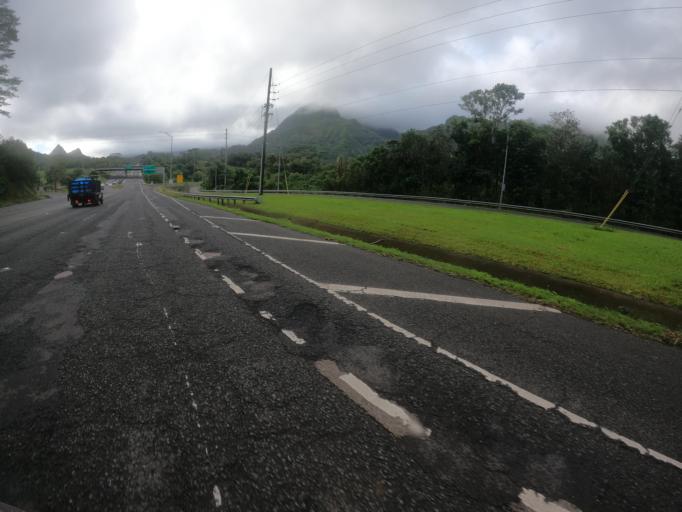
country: US
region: Hawaii
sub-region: Honolulu County
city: Kane'ohe
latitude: 21.3866
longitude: -157.7927
